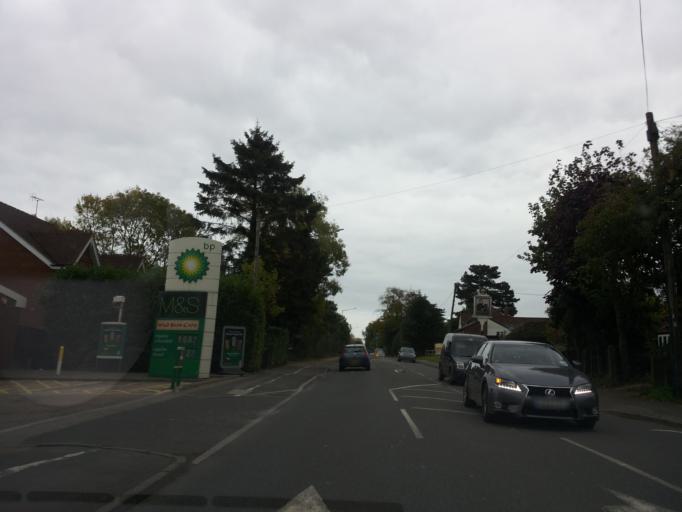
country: GB
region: England
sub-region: Buckinghamshire
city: Little Chalfont
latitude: 51.6713
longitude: -0.5835
